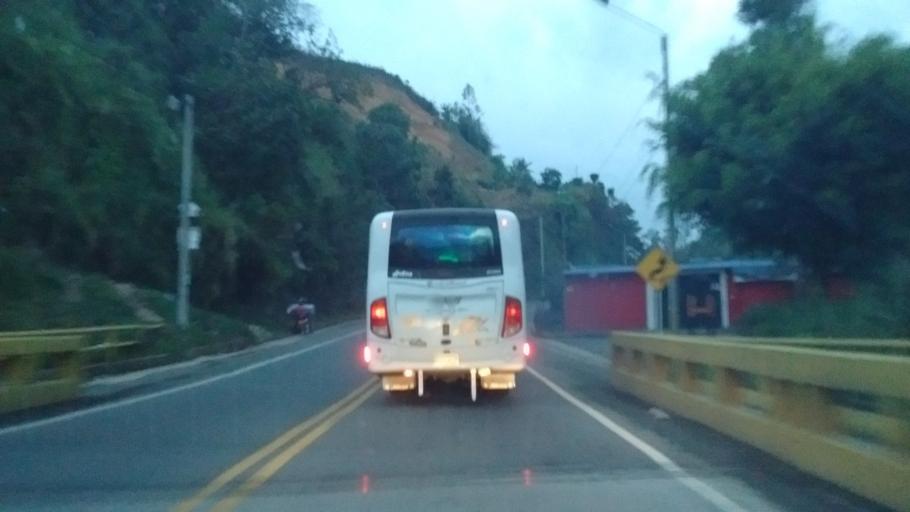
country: CO
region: Cauca
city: Popayan
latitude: 2.4245
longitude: -76.6266
